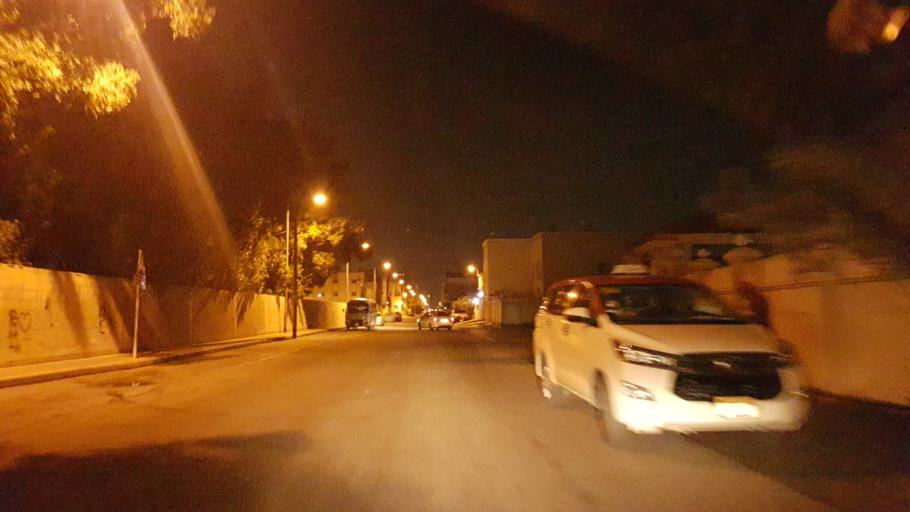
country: BH
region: Muharraq
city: Al Hadd
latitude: 26.2403
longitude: 50.6510
